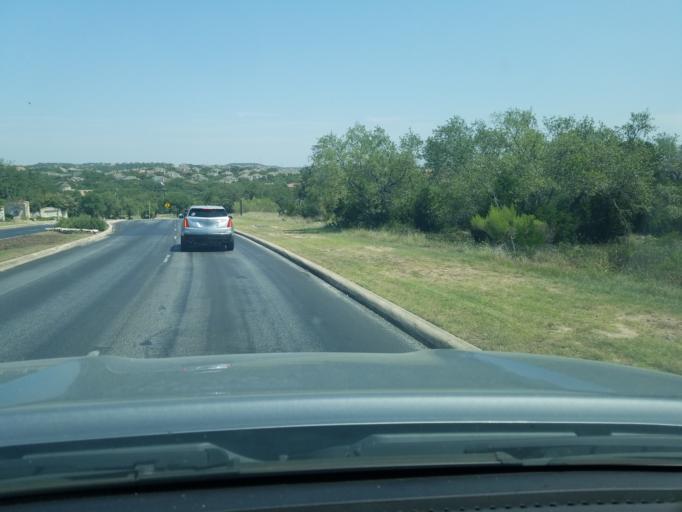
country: US
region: Texas
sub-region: Bexar County
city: Timberwood Park
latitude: 29.6636
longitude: -98.4782
